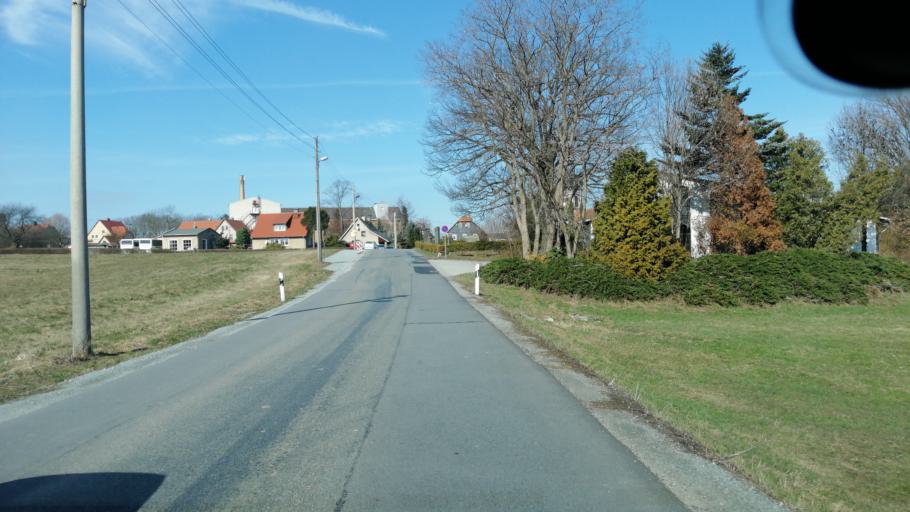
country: DE
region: Saxony
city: Schonbach
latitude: 51.0595
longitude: 14.5749
